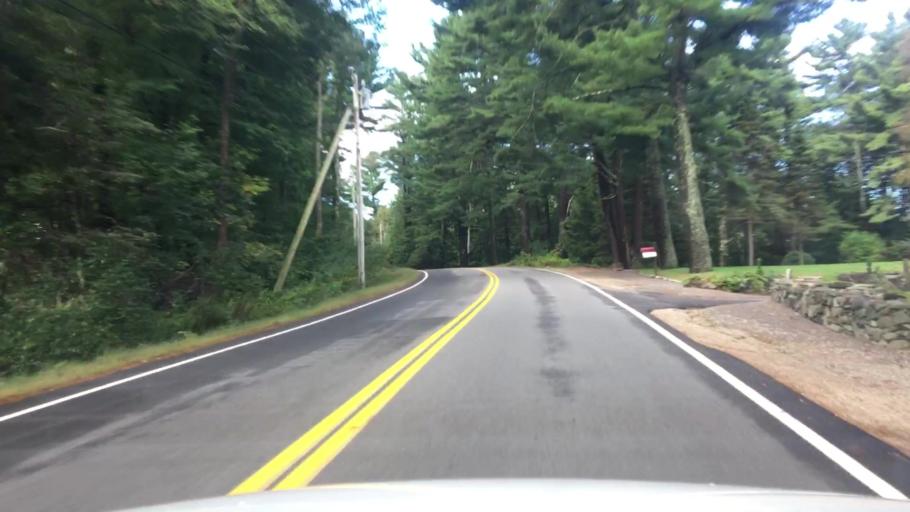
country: US
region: Maine
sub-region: York County
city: Kittery Point
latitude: 43.0898
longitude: -70.7036
